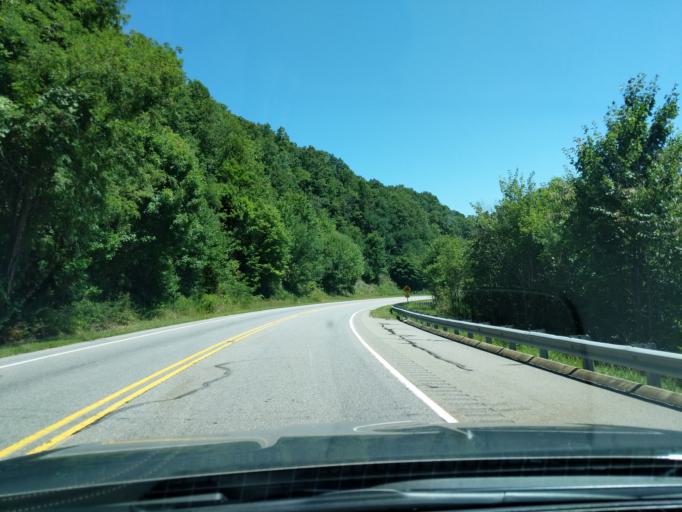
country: US
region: North Carolina
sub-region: Macon County
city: Franklin
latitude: 35.1307
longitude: -83.5199
